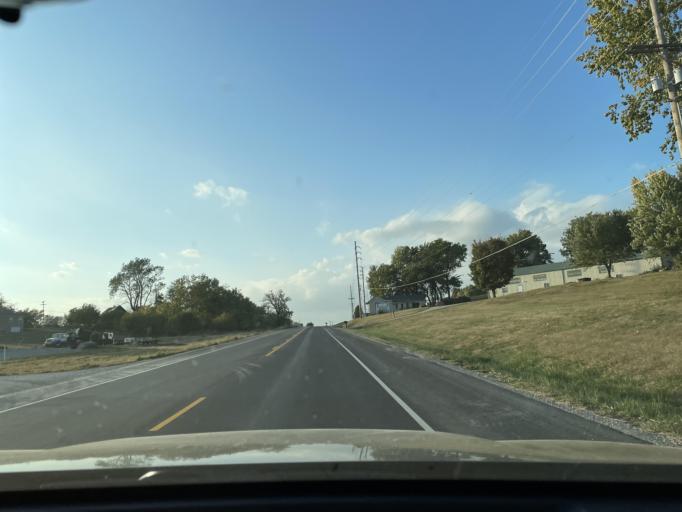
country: US
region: Missouri
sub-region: Andrew County
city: Country Club Village
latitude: 39.8276
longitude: -94.8574
